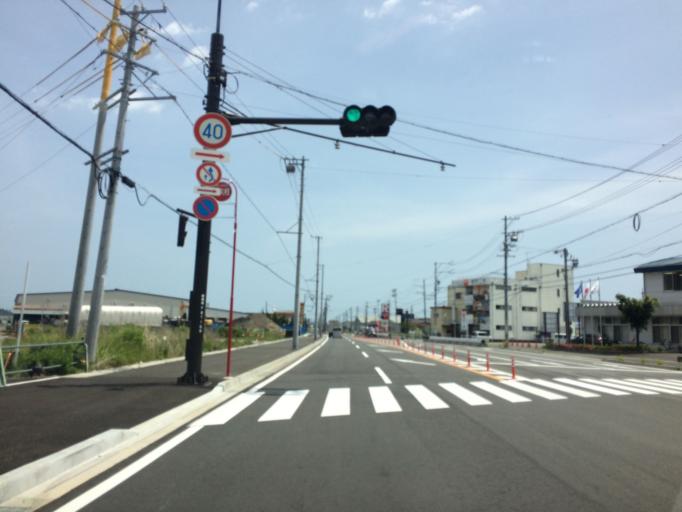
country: JP
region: Shizuoka
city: Fujieda
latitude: 34.8892
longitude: 138.2889
